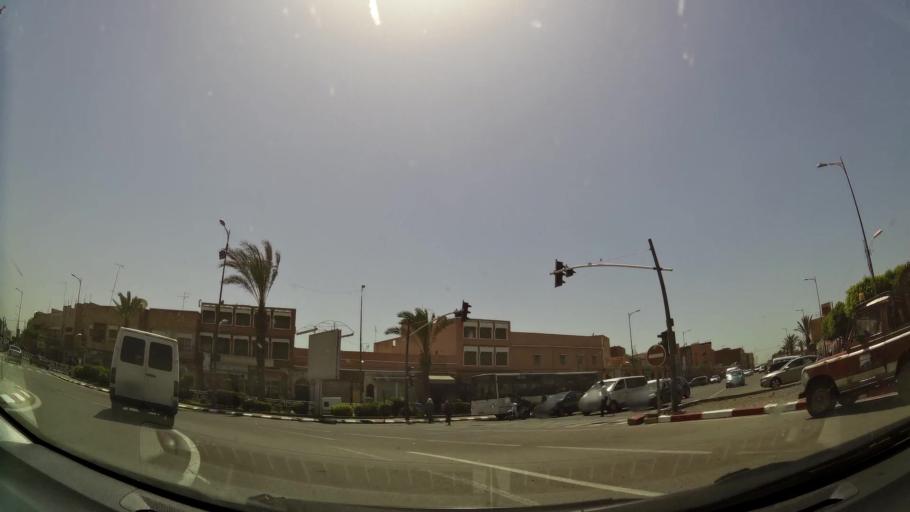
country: MA
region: Souss-Massa-Draa
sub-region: Inezgane-Ait Mellou
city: Inezgane
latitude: 30.3489
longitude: -9.5033
